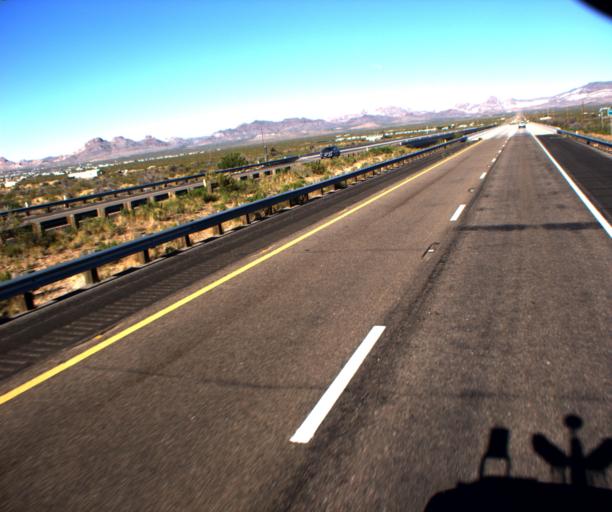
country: US
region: Arizona
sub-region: Mohave County
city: Golden Valley
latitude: 35.2252
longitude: -114.2783
